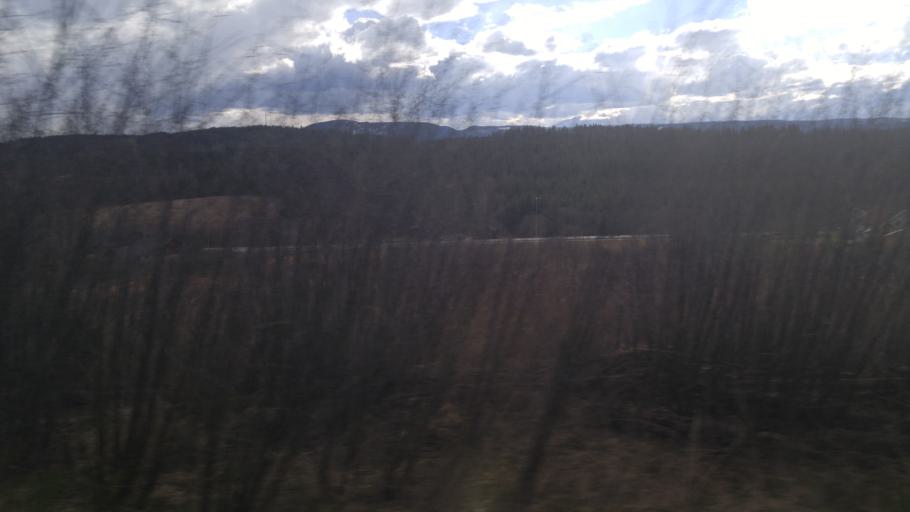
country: NO
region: Hedmark
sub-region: Stange
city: Stange
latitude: 60.6268
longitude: 11.2487
